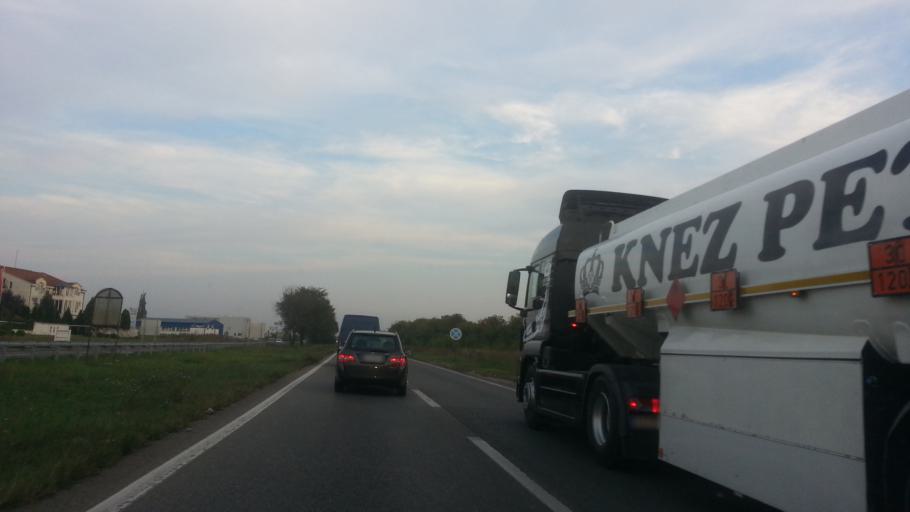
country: RS
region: Central Serbia
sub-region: Belgrade
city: Zemun
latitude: 44.8718
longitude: 20.3344
